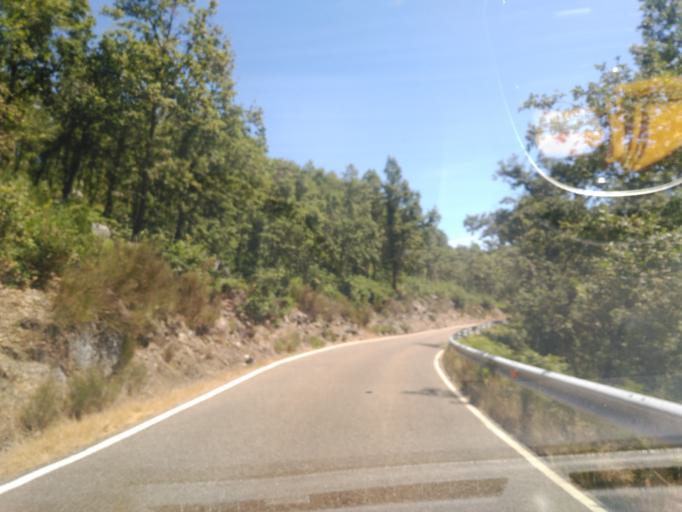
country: ES
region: Castille and Leon
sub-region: Provincia de Zamora
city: Galende
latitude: 42.1342
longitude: -6.7018
